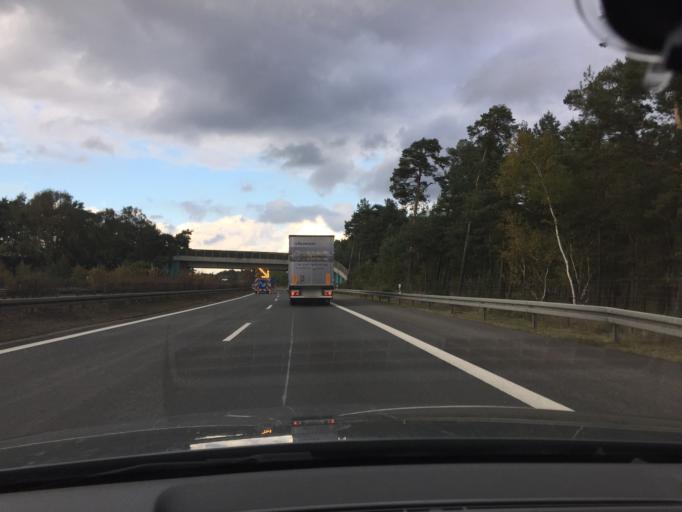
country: DE
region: Brandenburg
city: Grossraschen
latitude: 51.6032
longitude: 13.9540
